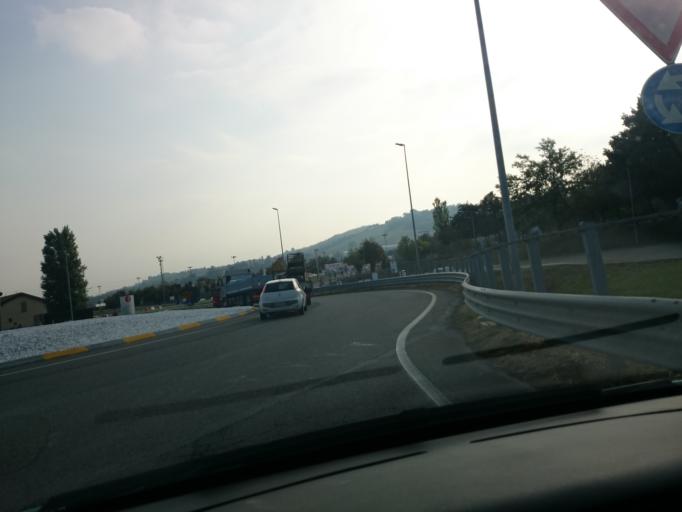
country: IT
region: Emilia-Romagna
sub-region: Provincia di Reggio Emilia
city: Casalgrande
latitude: 44.5802
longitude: 10.7418
